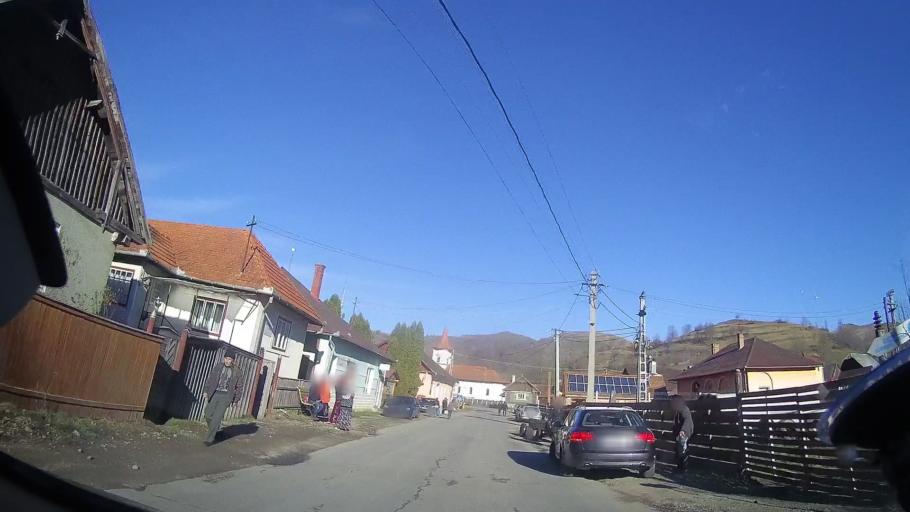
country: RO
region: Cluj
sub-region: Comuna Sacueu
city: Sacuieu
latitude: 46.8216
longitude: 22.8872
